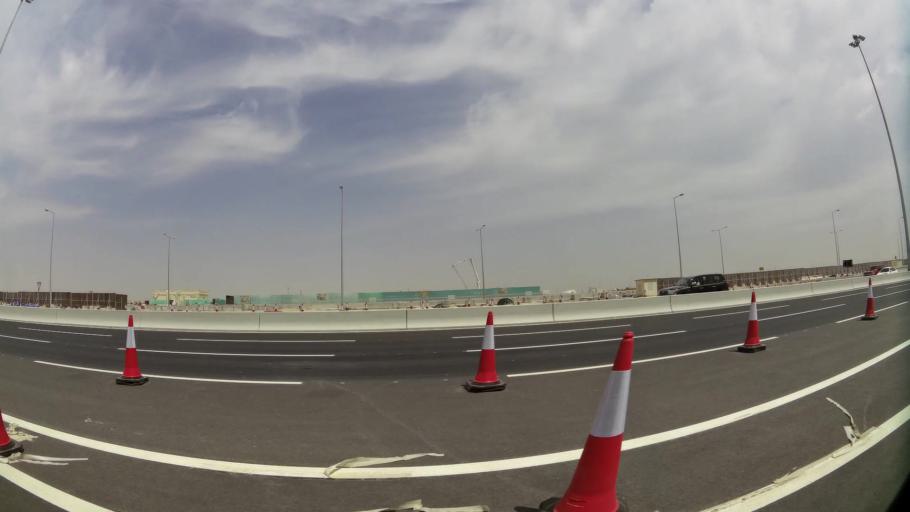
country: QA
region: Baladiyat ar Rayyan
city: Ar Rayyan
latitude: 25.3038
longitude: 51.4184
